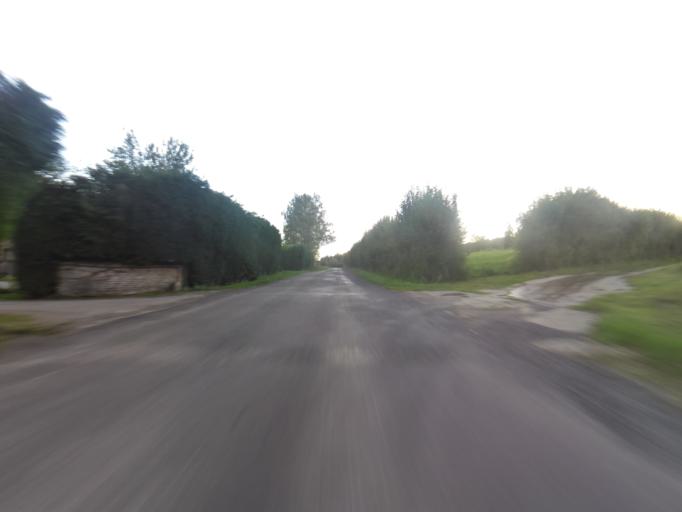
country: FR
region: Lower Normandy
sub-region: Departement de l'Orne
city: Vimoutiers
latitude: 48.9252
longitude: 0.2652
